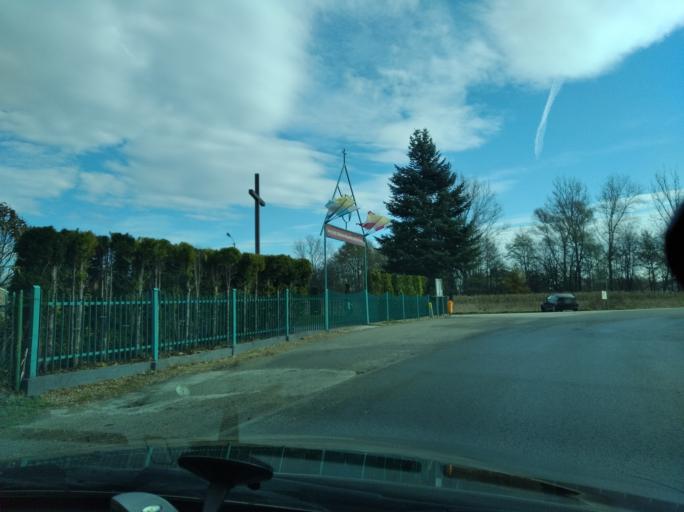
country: PL
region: Subcarpathian Voivodeship
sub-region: Powiat ropczycko-sedziszowski
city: Ostrow
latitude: 50.0964
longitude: 21.5537
